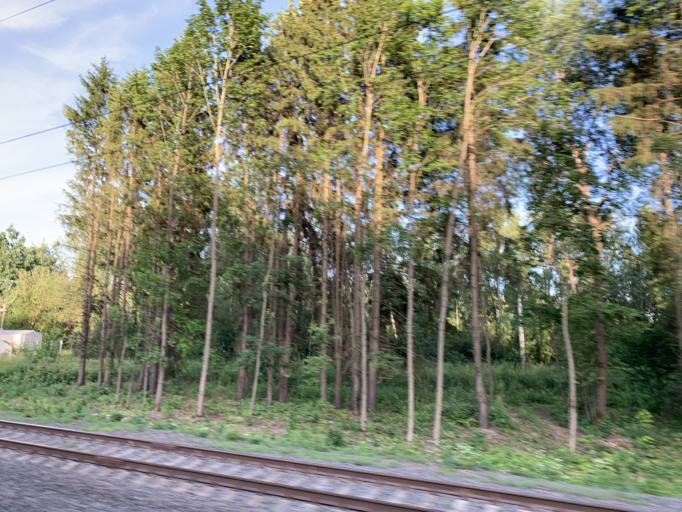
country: BY
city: Fanipol
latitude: 53.7547
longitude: 27.3574
